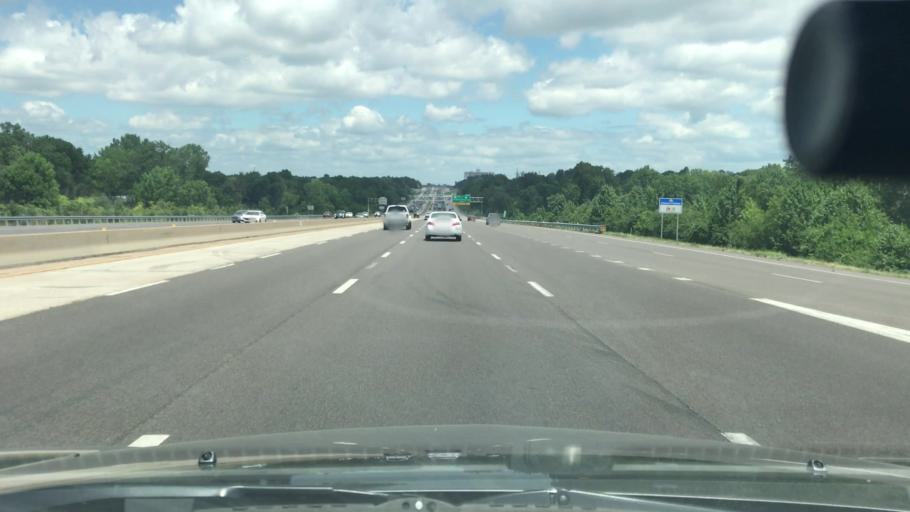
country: US
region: Missouri
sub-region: Saint Louis County
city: Creve Coeur
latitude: 38.6761
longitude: -90.4493
